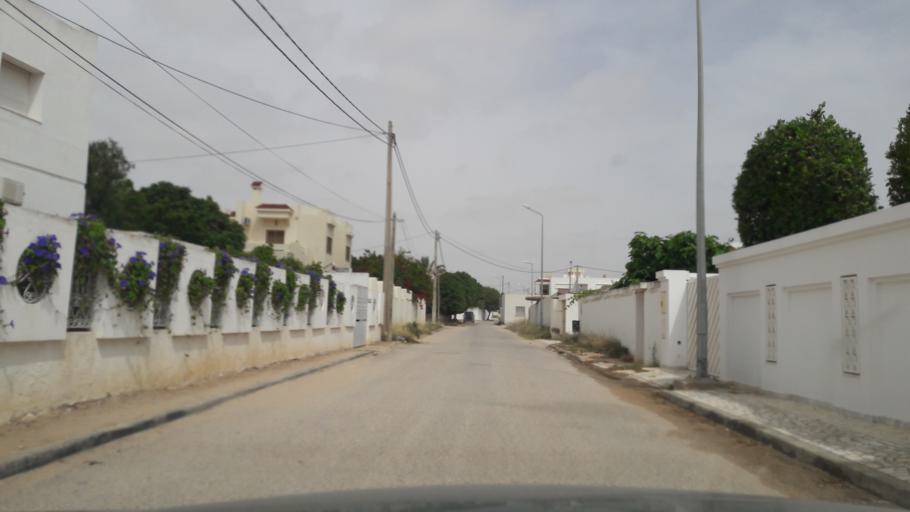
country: TN
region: Safaqis
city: Sfax
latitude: 34.7749
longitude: 10.7580
